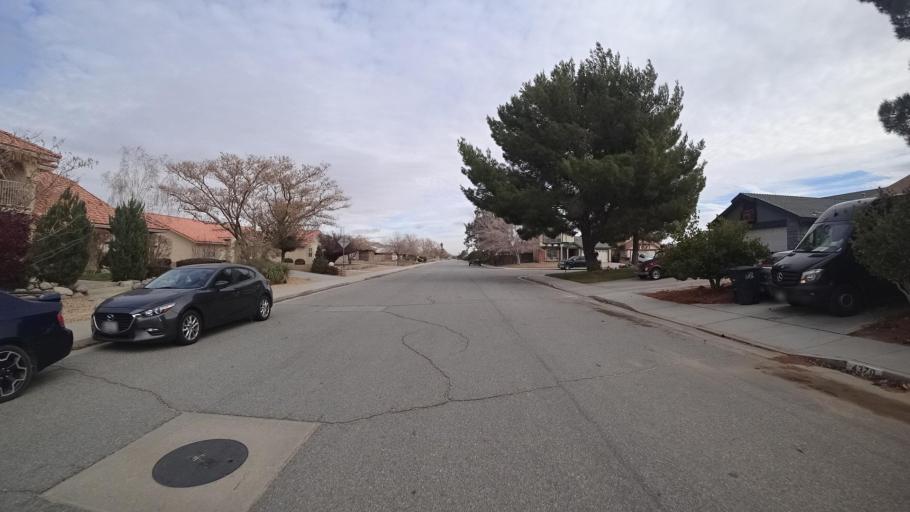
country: US
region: California
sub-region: Kern County
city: Rosamond
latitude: 34.8674
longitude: -118.2091
